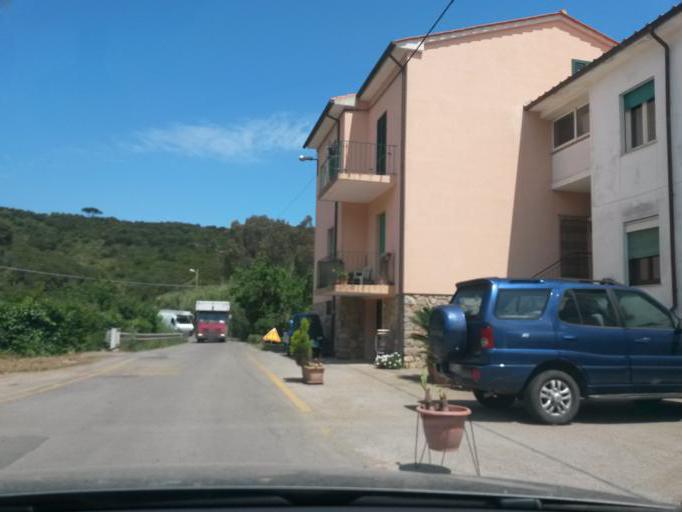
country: IT
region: Tuscany
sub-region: Provincia di Livorno
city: Rio Marina
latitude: 42.8122
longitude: 10.4150
